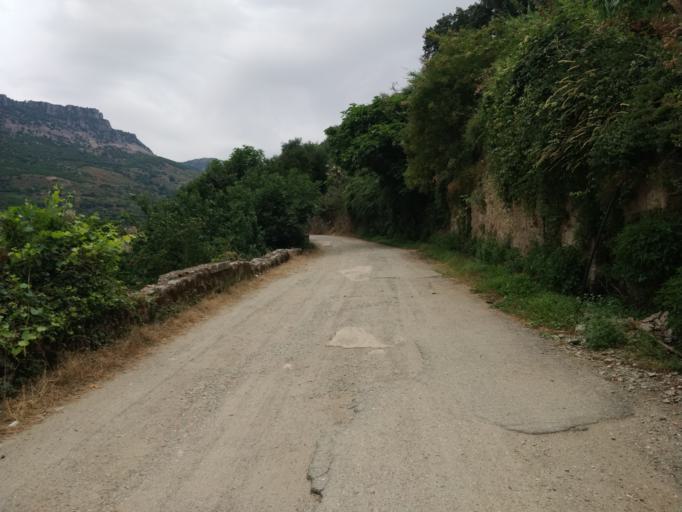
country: IT
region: Sardinia
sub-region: Provincia di Ogliastra
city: Gairo Sant'Elena
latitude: 39.8483
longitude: 9.4995
